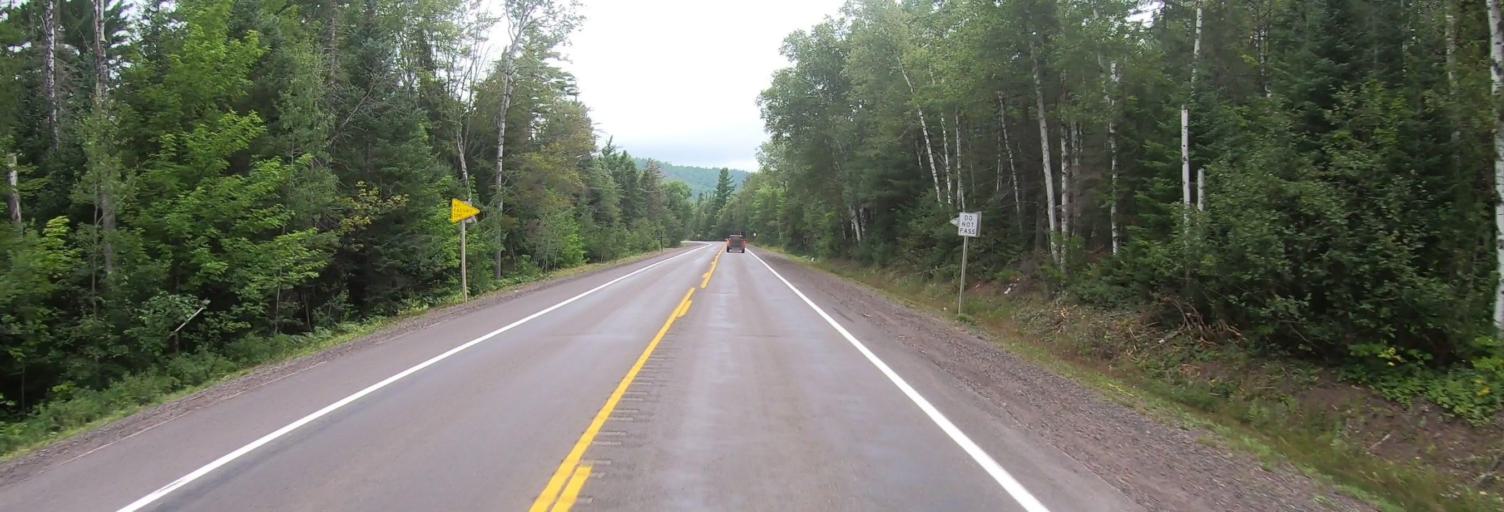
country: US
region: Michigan
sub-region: Keweenaw County
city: Eagle River
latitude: 47.3698
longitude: -88.3060
